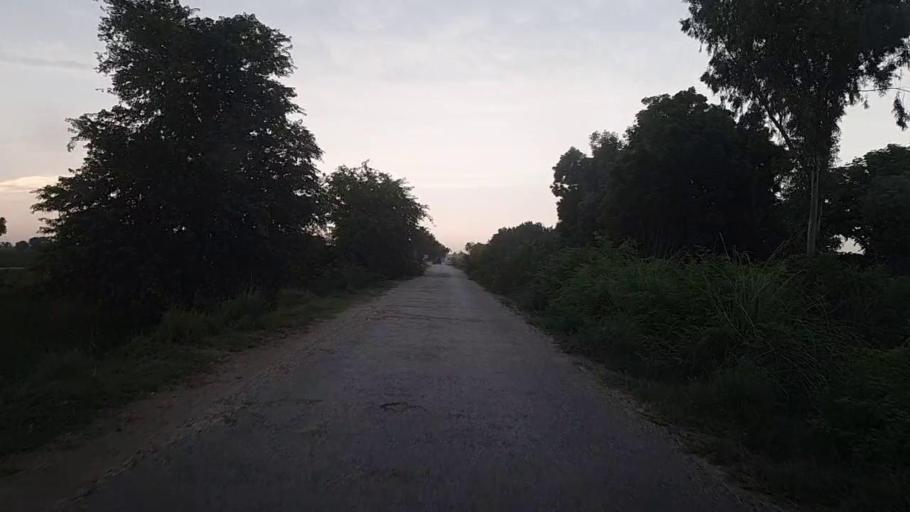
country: PK
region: Sindh
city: Karaundi
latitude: 27.0211
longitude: 68.3480
